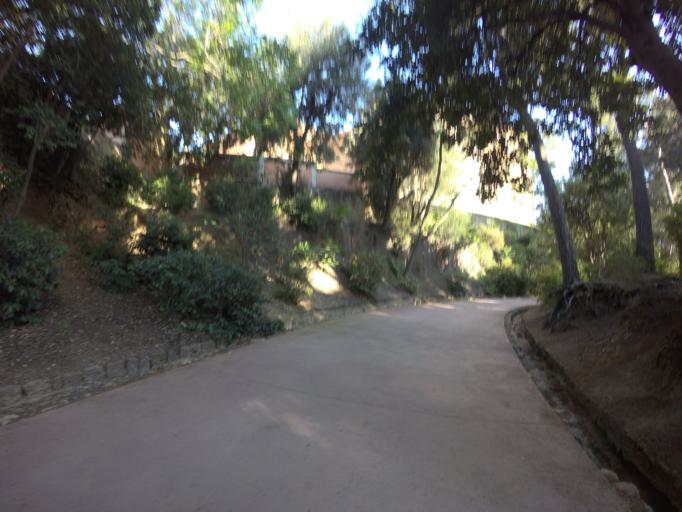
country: ES
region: Catalonia
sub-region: Provincia de Barcelona
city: Gracia
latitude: 41.4148
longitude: 2.1548
